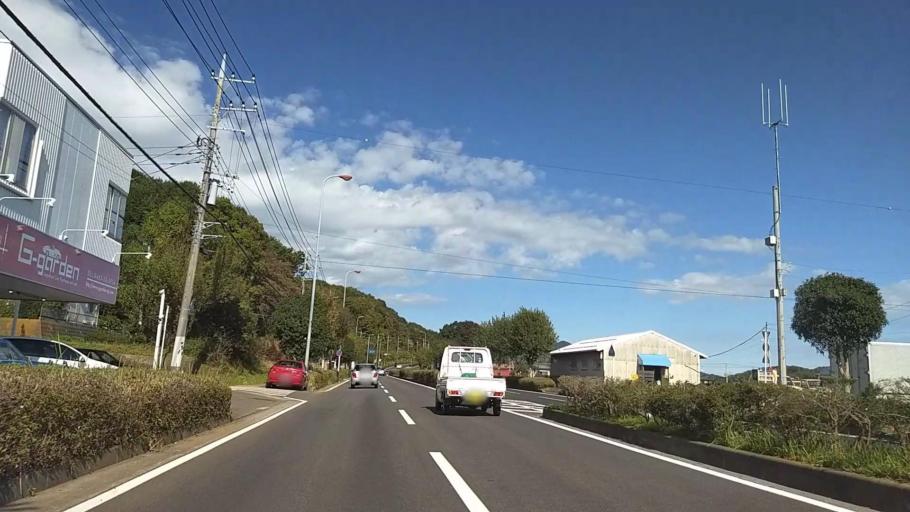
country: JP
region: Kanagawa
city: Hadano
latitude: 35.3410
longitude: 139.2302
